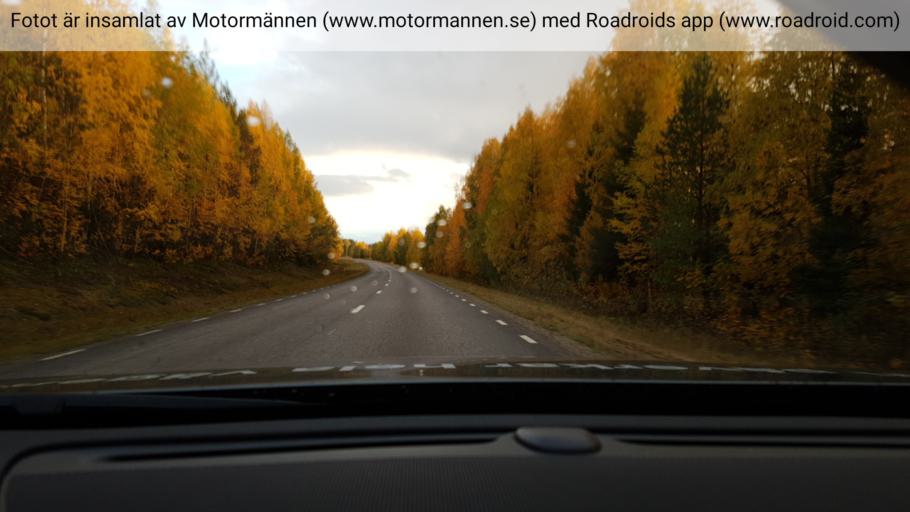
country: SE
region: Norrbotten
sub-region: Overkalix Kommun
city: OEverkalix
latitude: 66.5438
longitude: 22.7544
